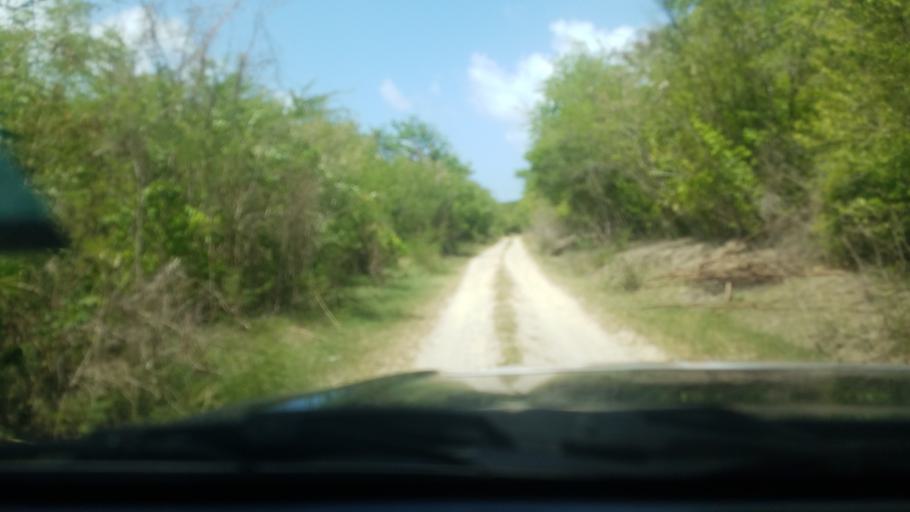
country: LC
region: Vieux-Fort
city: Vieux Fort
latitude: 13.7509
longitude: -60.9413
